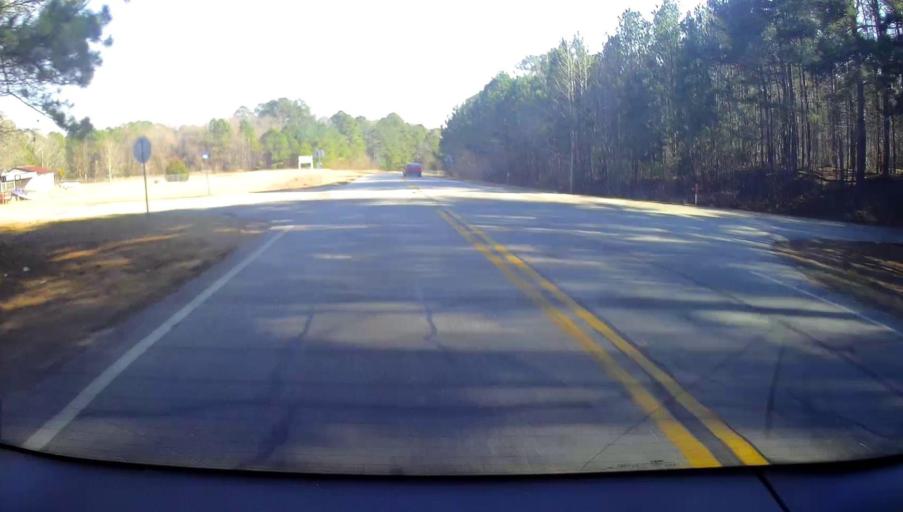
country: US
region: Georgia
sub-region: Butts County
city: Indian Springs
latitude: 33.2479
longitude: -83.8881
